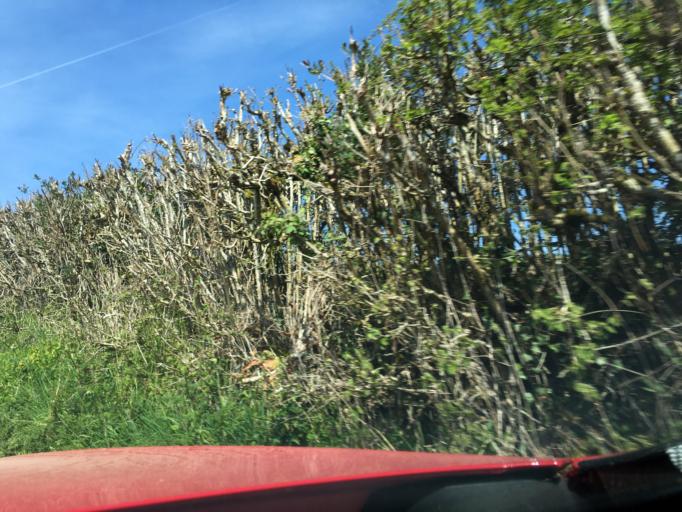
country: GB
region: Wales
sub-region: Monmouthshire
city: Llangwm
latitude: 51.7381
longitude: -2.8220
